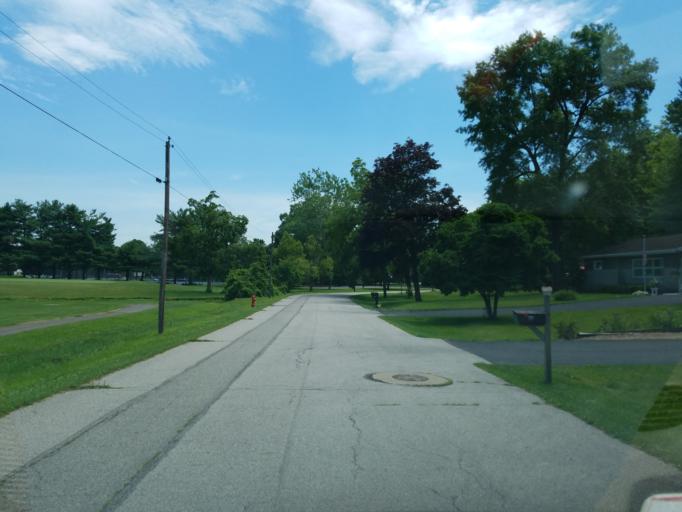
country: US
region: Ohio
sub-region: Ashland County
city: Ashland
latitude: 40.8748
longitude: -82.3329
